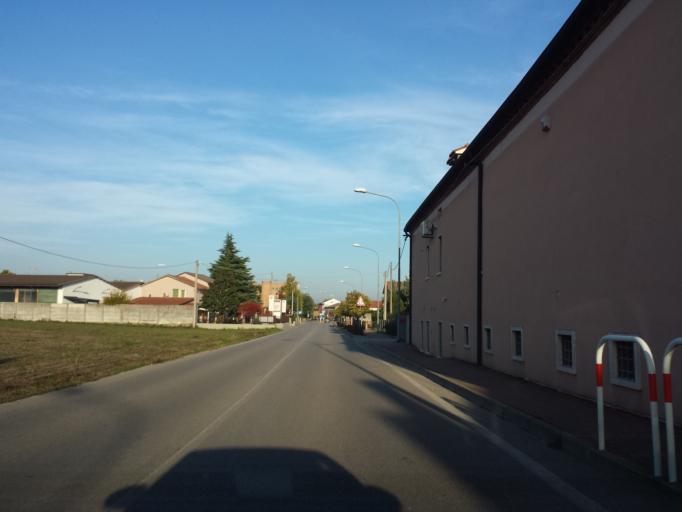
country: IT
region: Veneto
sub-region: Provincia di Vicenza
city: Crispi Cavour
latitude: 45.5896
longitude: 11.5193
